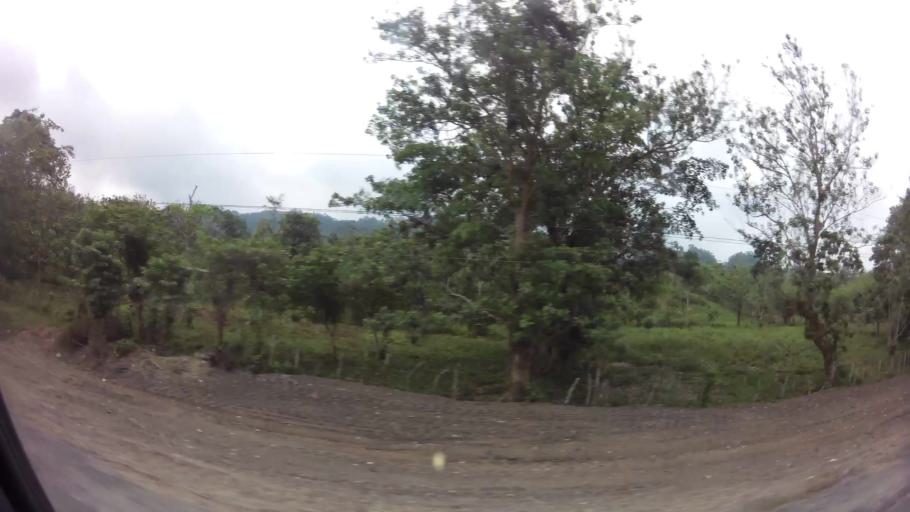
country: HN
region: Yoro
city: Guaimitas
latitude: 15.4953
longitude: -87.7219
